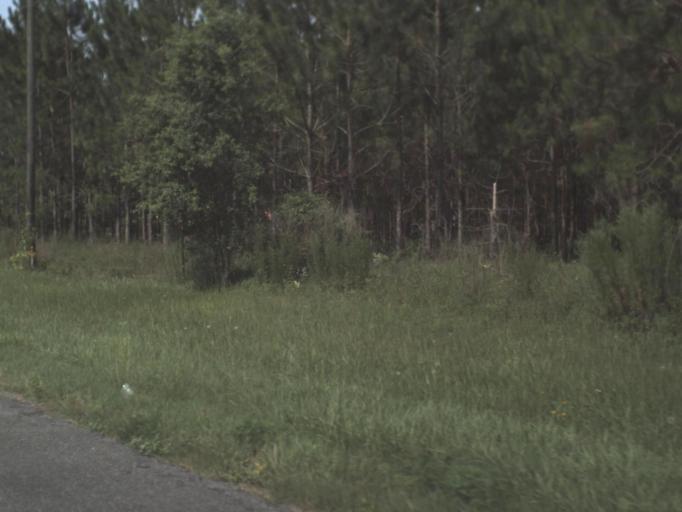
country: US
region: Florida
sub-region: Lafayette County
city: Mayo
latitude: 30.0737
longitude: -83.1741
